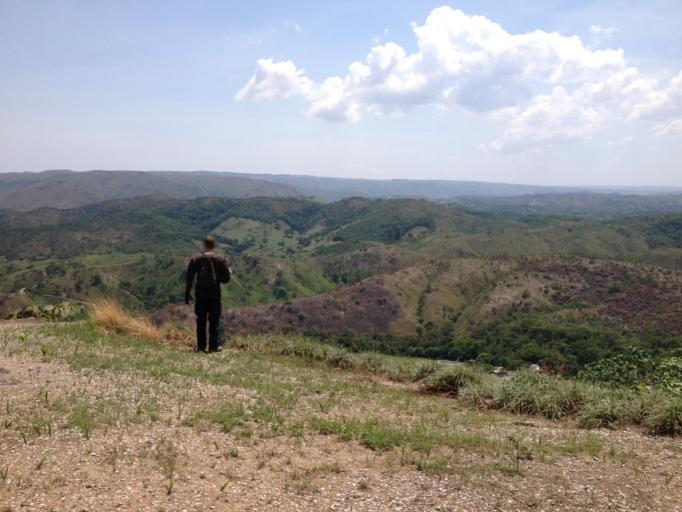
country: BR
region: Federal District
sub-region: Brasilia
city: Brasilia
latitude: -15.6600
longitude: -48.3804
